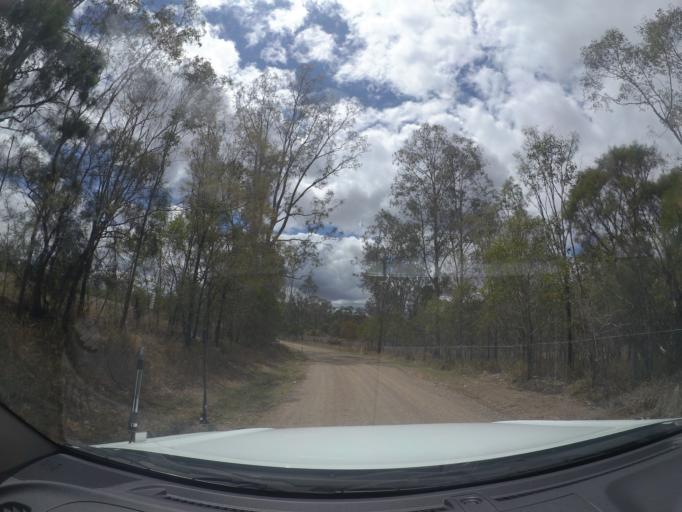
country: AU
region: Queensland
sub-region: Logan
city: Cedar Vale
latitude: -27.8299
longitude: 153.0360
